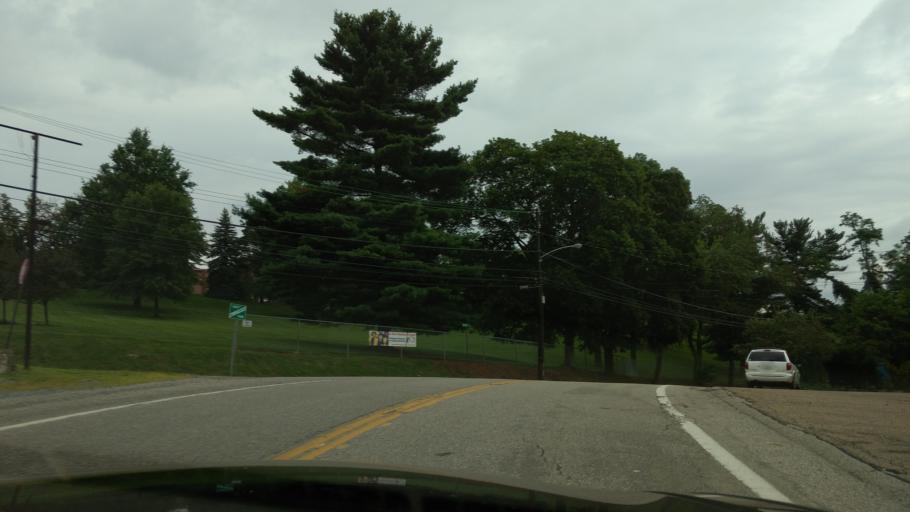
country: US
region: Pennsylvania
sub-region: Allegheny County
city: Bellevue
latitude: 40.5058
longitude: -80.0489
